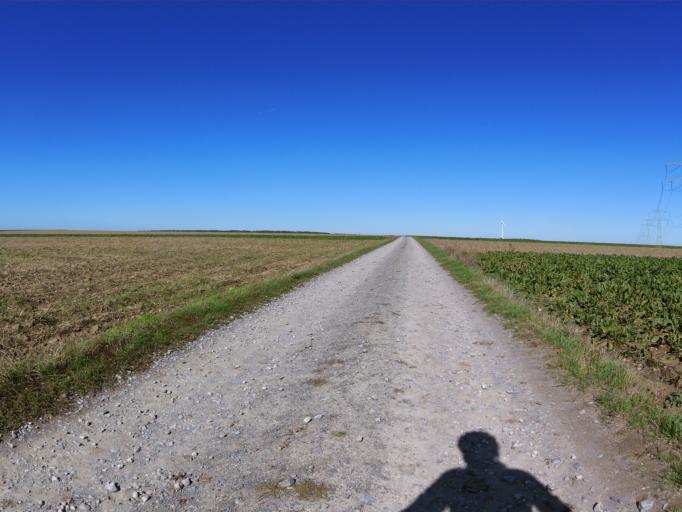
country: DE
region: Bavaria
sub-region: Regierungsbezirk Unterfranken
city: Theilheim
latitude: 49.7292
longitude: 10.0473
